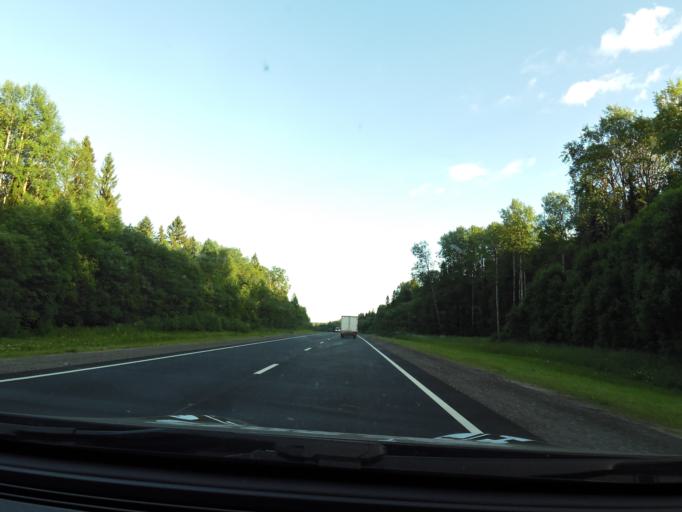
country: RU
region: Vologda
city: Gryazovets
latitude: 58.9213
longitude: 40.1765
